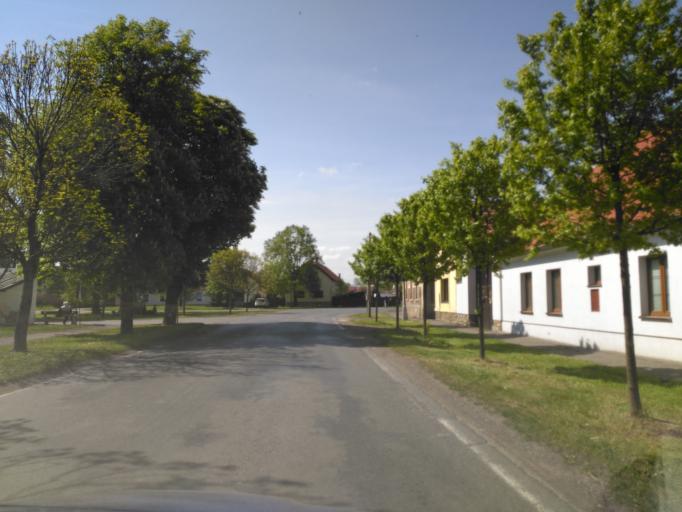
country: CZ
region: Central Bohemia
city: Lochovice
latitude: 49.8712
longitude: 13.9977
